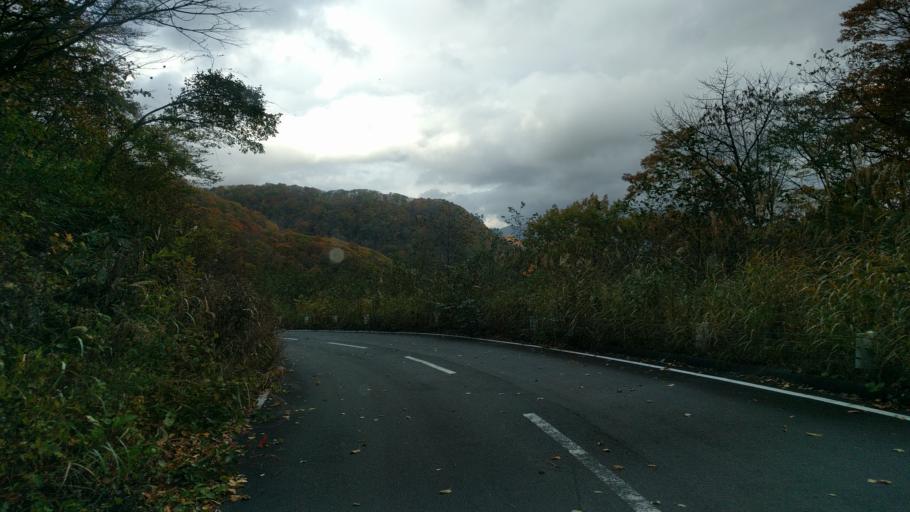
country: JP
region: Fukushima
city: Kitakata
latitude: 37.3788
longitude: 139.7147
